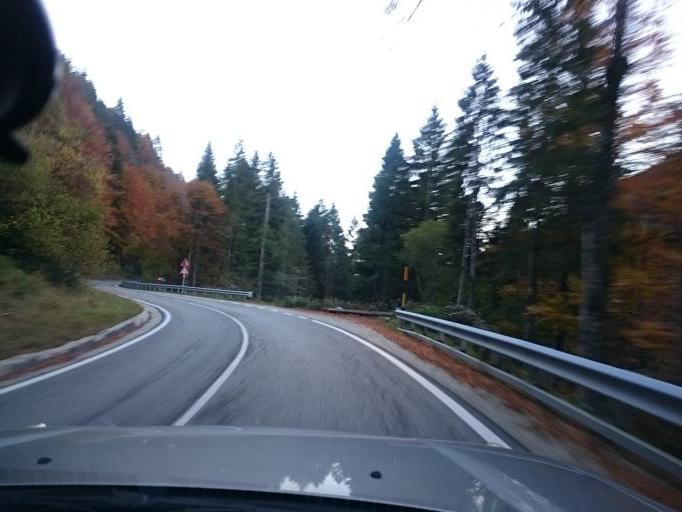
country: IT
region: Veneto
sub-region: Provincia di Vicenza
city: Roana
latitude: 45.9048
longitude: 11.4601
